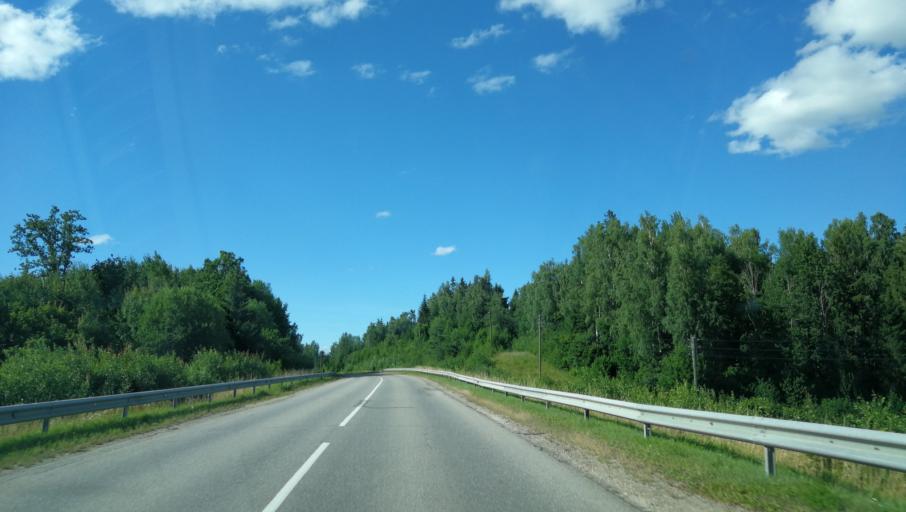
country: LV
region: Madonas Rajons
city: Madona
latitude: 56.8738
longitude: 26.1793
